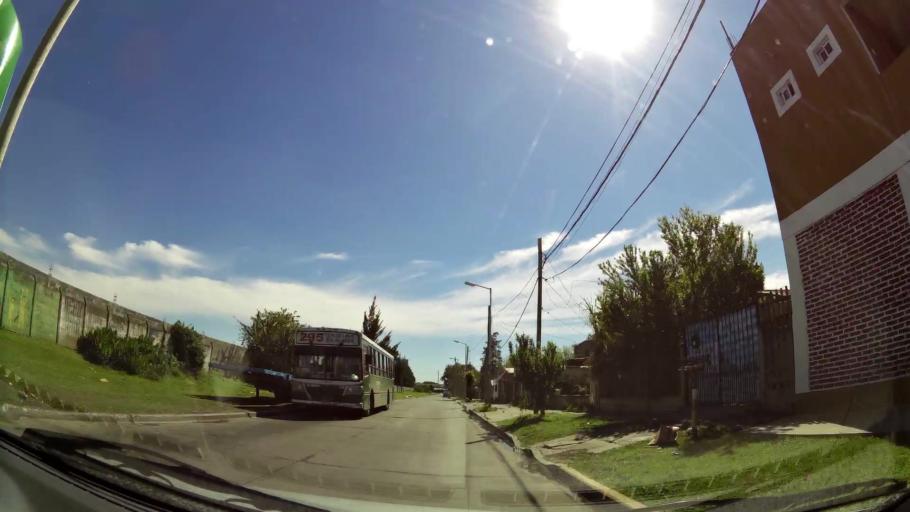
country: AR
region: Buenos Aires
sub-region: Partido de Avellaneda
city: Avellaneda
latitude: -34.6869
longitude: -58.3110
